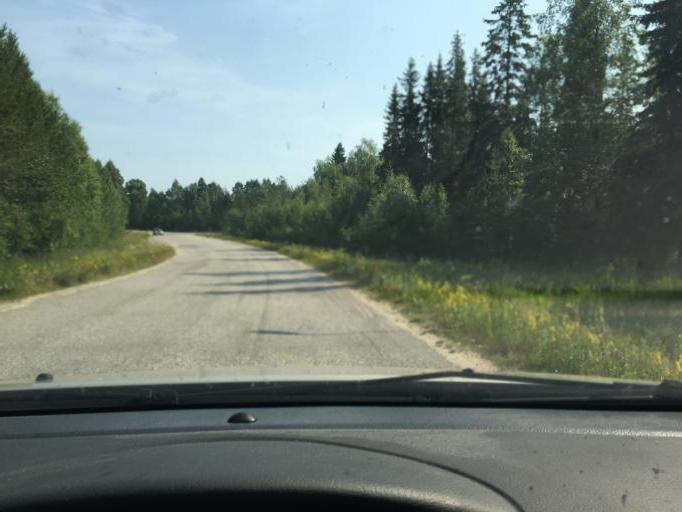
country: SE
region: Norrbotten
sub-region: Kalix Kommun
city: Kalix
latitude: 65.7770
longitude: 23.1893
